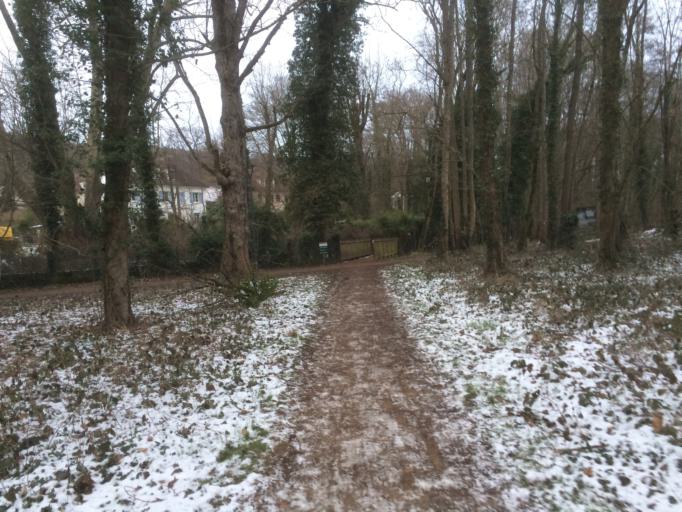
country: FR
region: Ile-de-France
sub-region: Departement de l'Essonne
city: Gif-sur-Yvette
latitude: 48.7006
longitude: 2.1375
